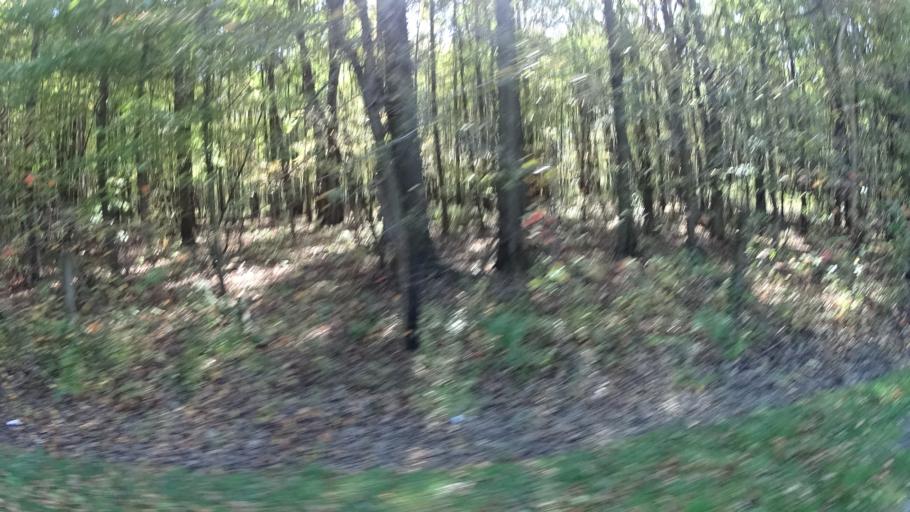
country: US
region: Ohio
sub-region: Lorain County
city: Vermilion-on-the-Lake
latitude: 41.4119
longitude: -82.3243
